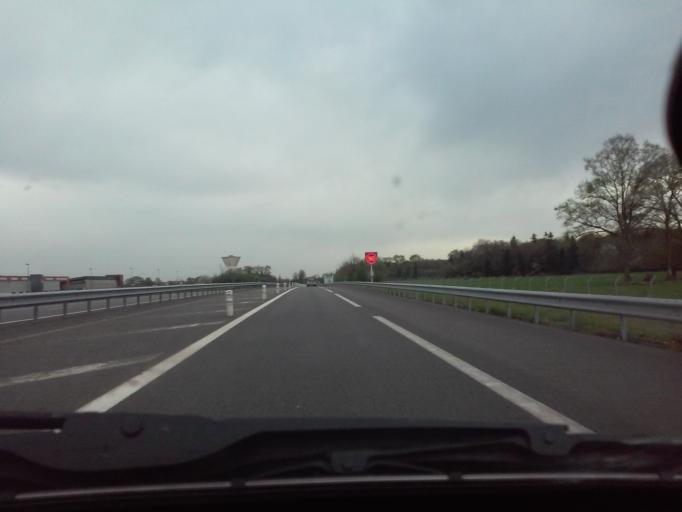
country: FR
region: Brittany
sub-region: Departement d'Ille-et-Vilaine
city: Romagne
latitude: 48.3459
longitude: -1.2873
